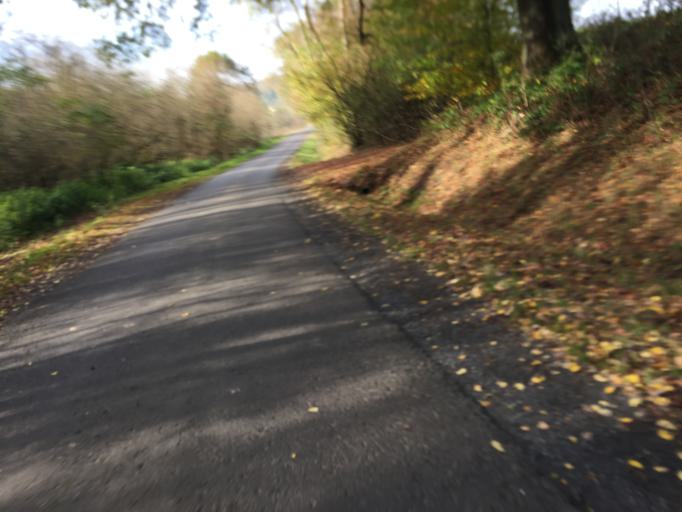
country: DE
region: Hesse
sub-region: Regierungsbezirk Giessen
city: Reiskirchen
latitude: 50.6039
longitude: 8.8717
